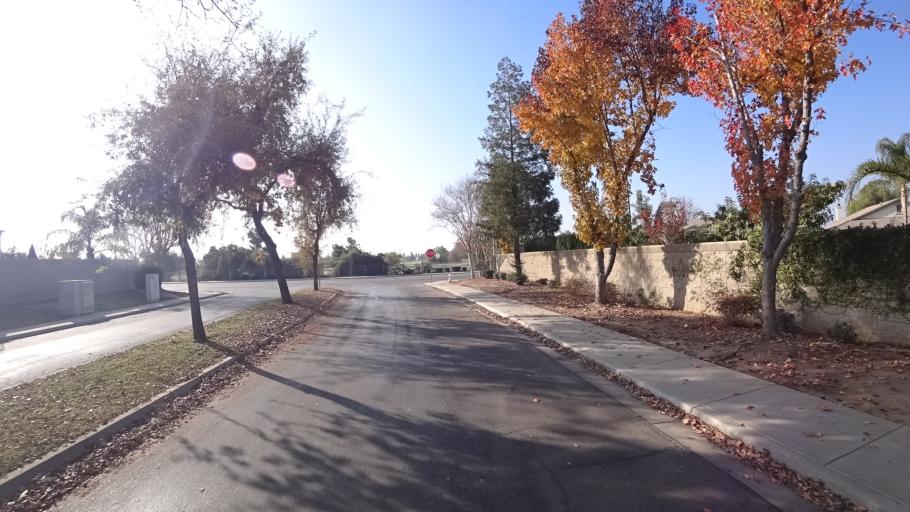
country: US
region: California
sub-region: Kern County
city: Greenacres
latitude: 35.4152
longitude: -119.1007
